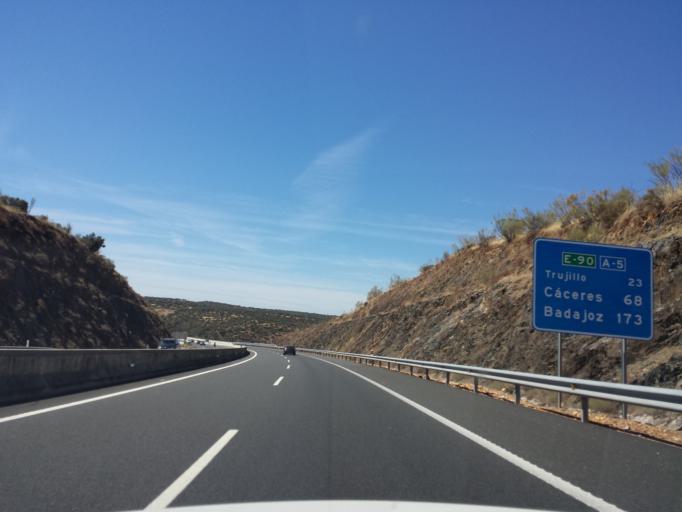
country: ES
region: Extremadura
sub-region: Provincia de Caceres
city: Jaraicejo
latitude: 39.6535
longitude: -5.8048
